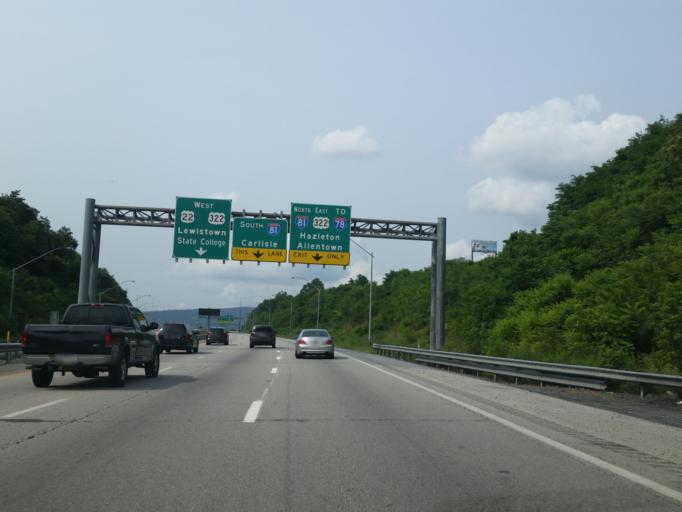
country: US
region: Pennsylvania
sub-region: Dauphin County
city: Harrisburg
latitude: 40.2921
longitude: -76.8813
